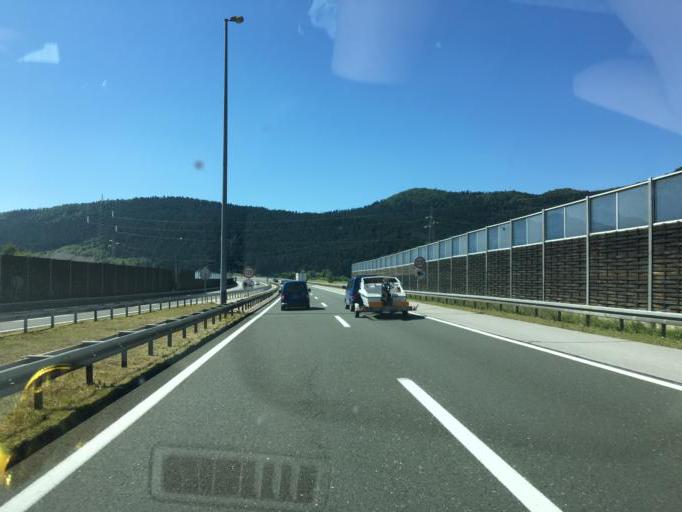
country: HR
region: Licko-Senjska
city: Otocac
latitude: 44.8697
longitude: 15.2075
